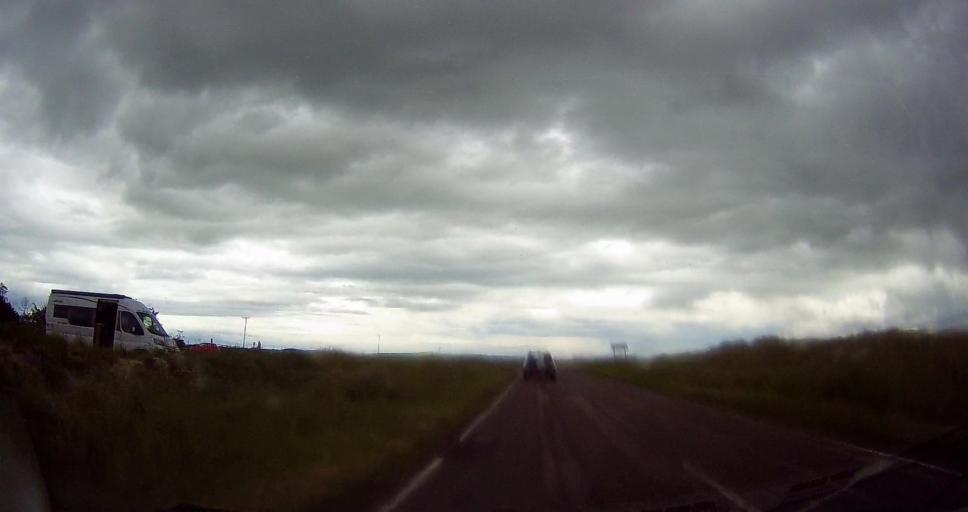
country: GB
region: Scotland
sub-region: Highland
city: Thurso
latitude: 58.6103
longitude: -3.3432
